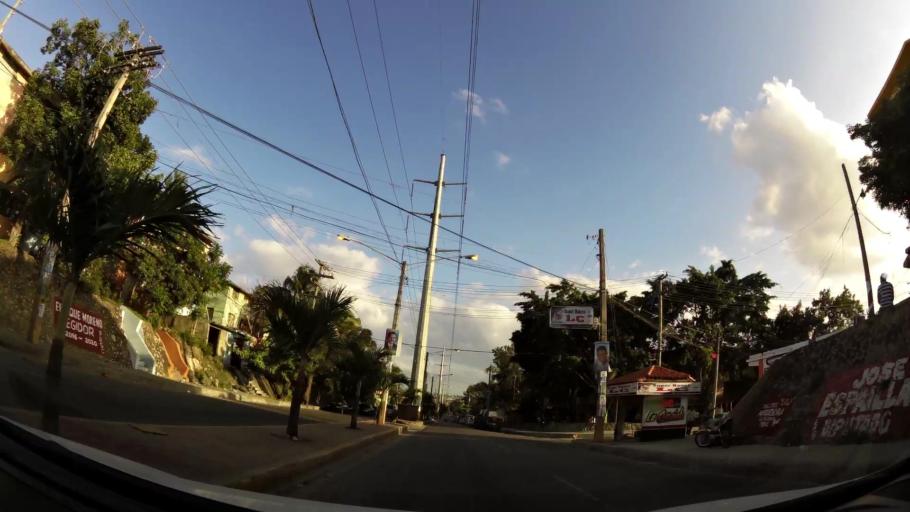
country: DO
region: Nacional
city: La Agustina
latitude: 18.5438
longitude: -69.9287
